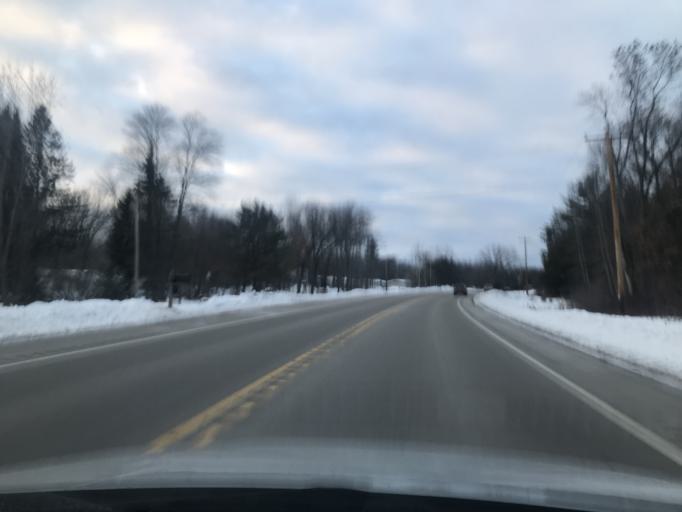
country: US
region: Wisconsin
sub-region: Marinette County
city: Peshtigo
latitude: 45.1611
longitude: -87.7228
